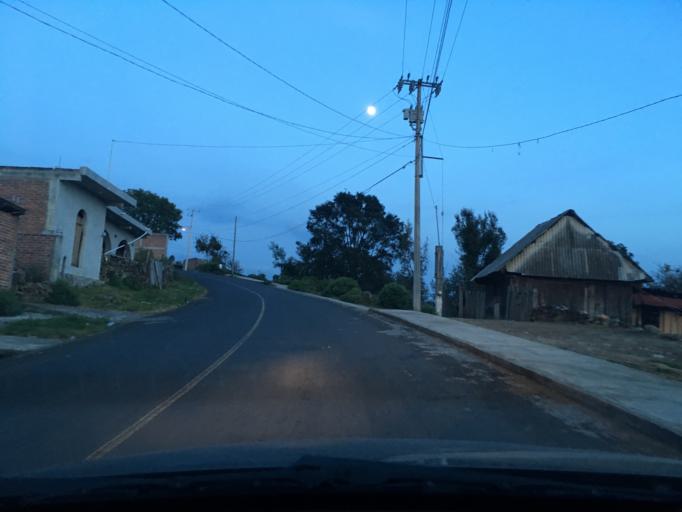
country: MX
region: Michoacan
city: Charapan
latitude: 19.6902
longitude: -102.1911
